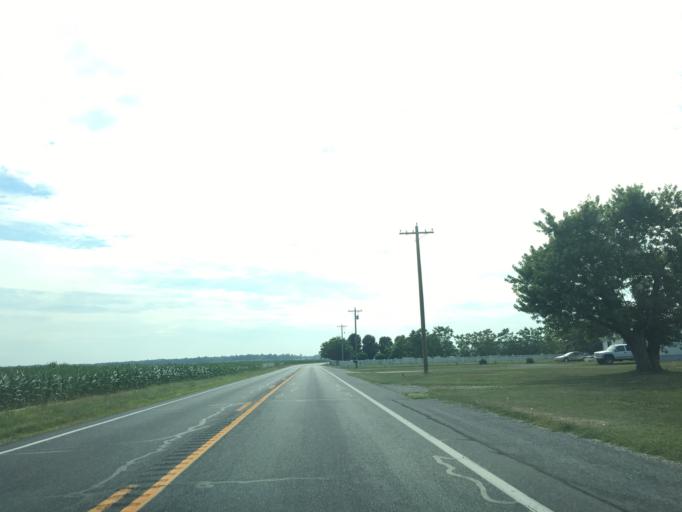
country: US
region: Delaware
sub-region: Sussex County
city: Bridgeville
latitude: 38.7546
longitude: -75.5042
